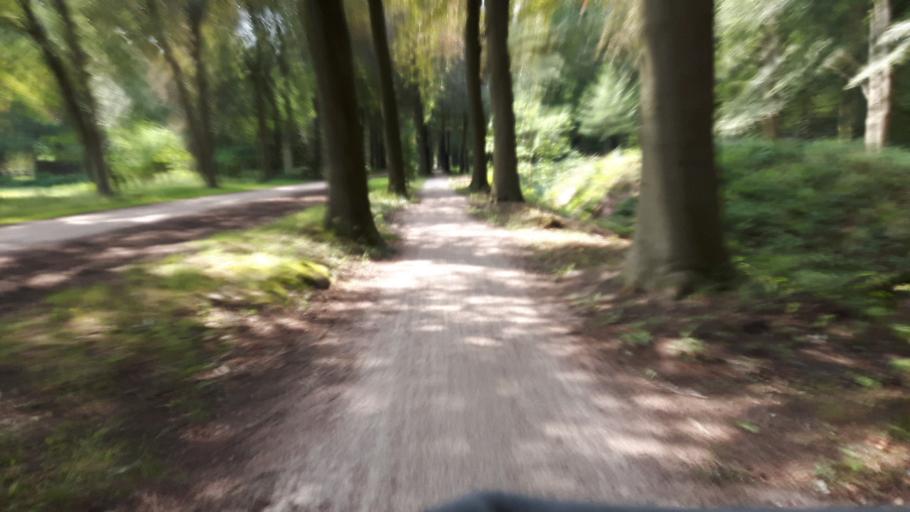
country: NL
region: Utrecht
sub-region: Gemeente Soest
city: Soest
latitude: 52.1775
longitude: 5.2330
